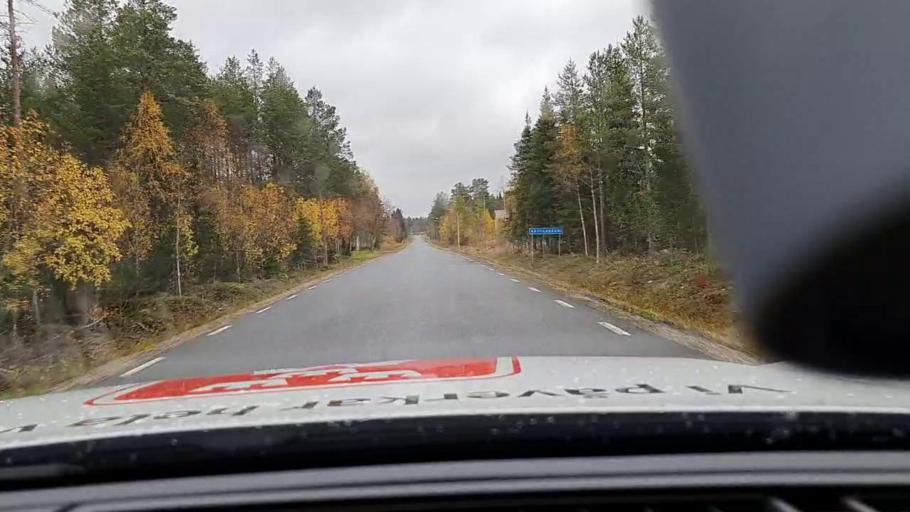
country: SE
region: Norrbotten
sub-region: Haparanda Kommun
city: Haparanda
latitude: 65.9427
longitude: 23.8010
